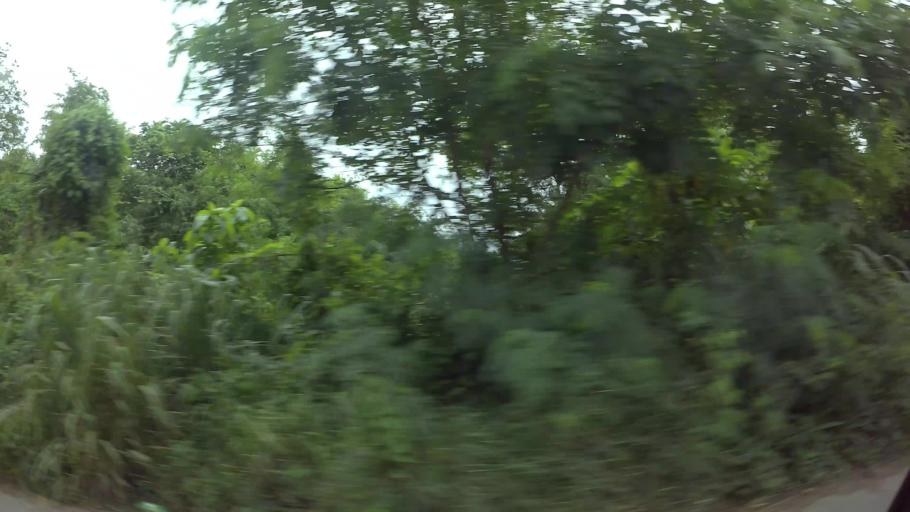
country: TH
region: Chon Buri
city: Si Racha
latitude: 13.1867
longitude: 100.9815
